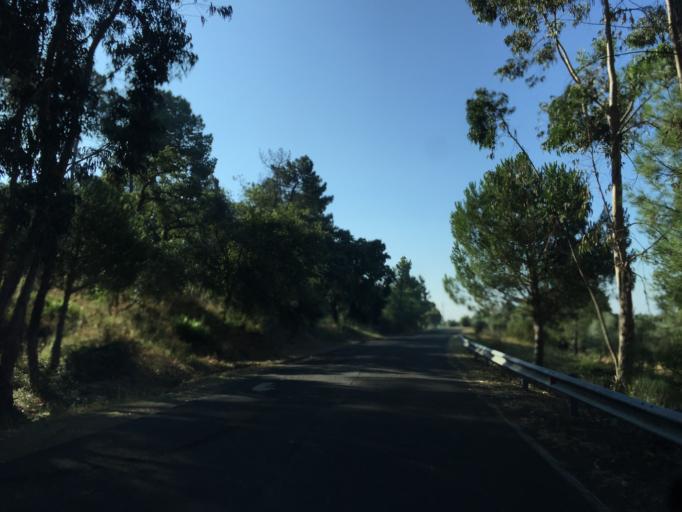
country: PT
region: Santarem
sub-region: Abrantes
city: Alferrarede
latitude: 39.5214
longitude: -8.1439
